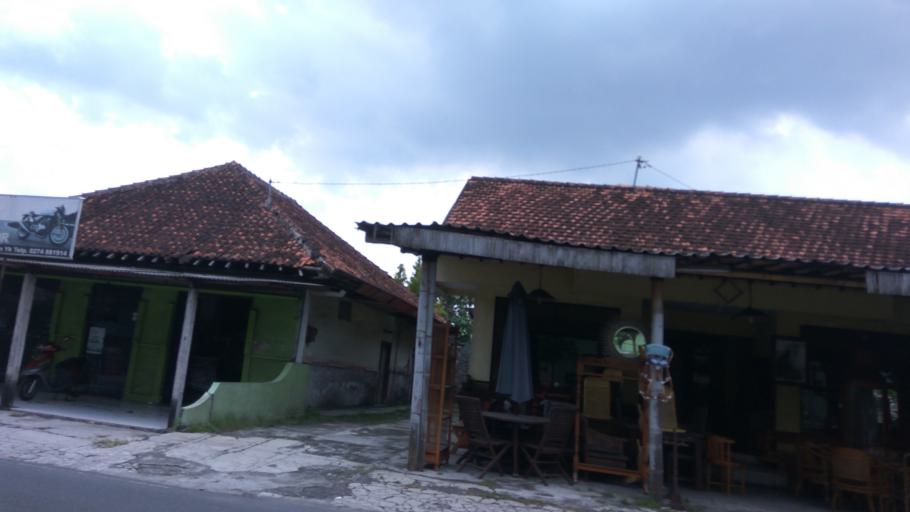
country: ID
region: Daerah Istimewa Yogyakarta
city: Melati
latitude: -7.7220
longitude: 110.4025
